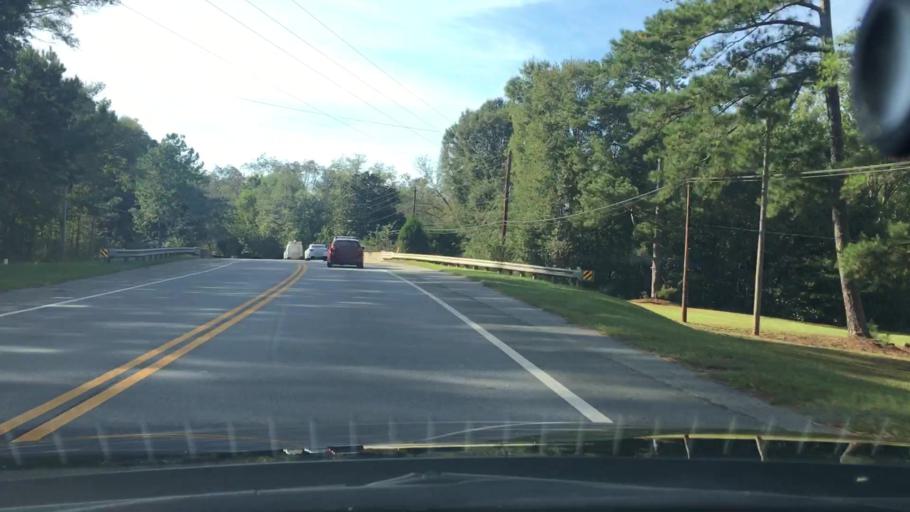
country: US
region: Georgia
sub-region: Coweta County
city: Senoia
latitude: 33.2958
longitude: -84.5483
